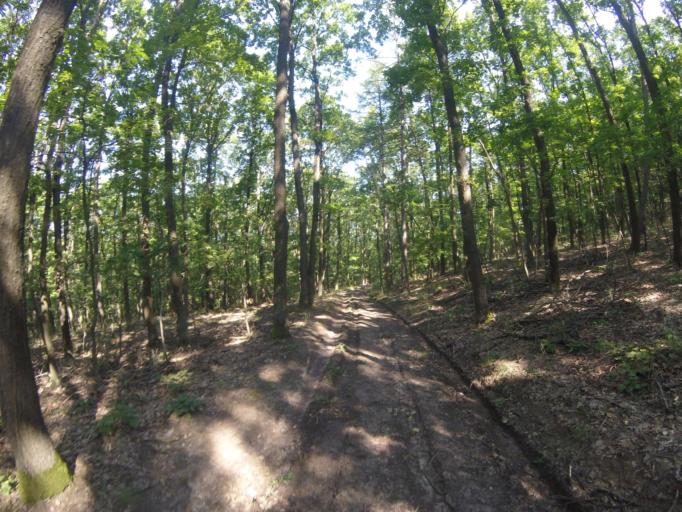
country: HU
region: Nograd
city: Bujak
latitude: 47.8917
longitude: 19.5251
